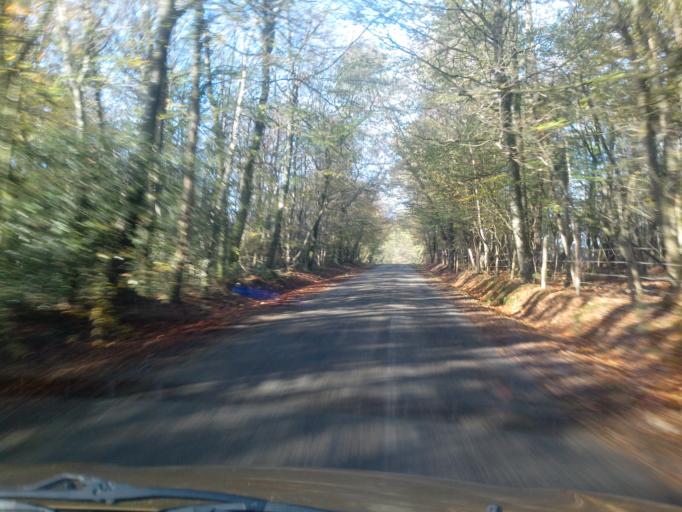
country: FR
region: Brittany
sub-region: Departement du Morbihan
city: Pluherlin
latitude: 47.7255
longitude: -2.3796
